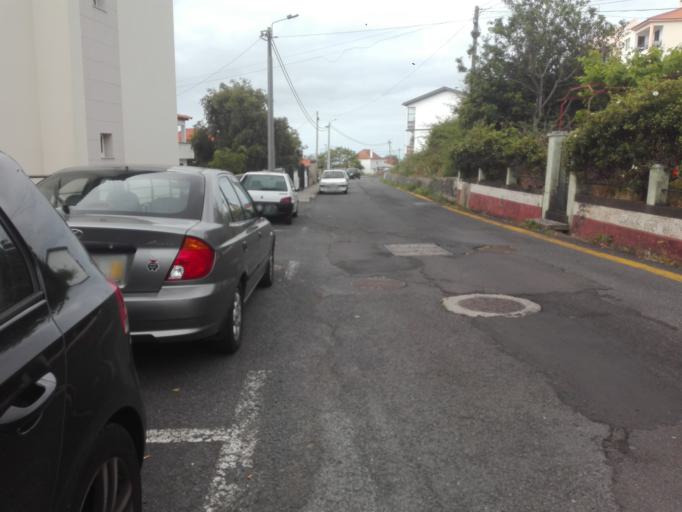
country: PT
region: Madeira
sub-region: Santa Cruz
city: Camacha
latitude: 32.6555
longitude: -16.8283
